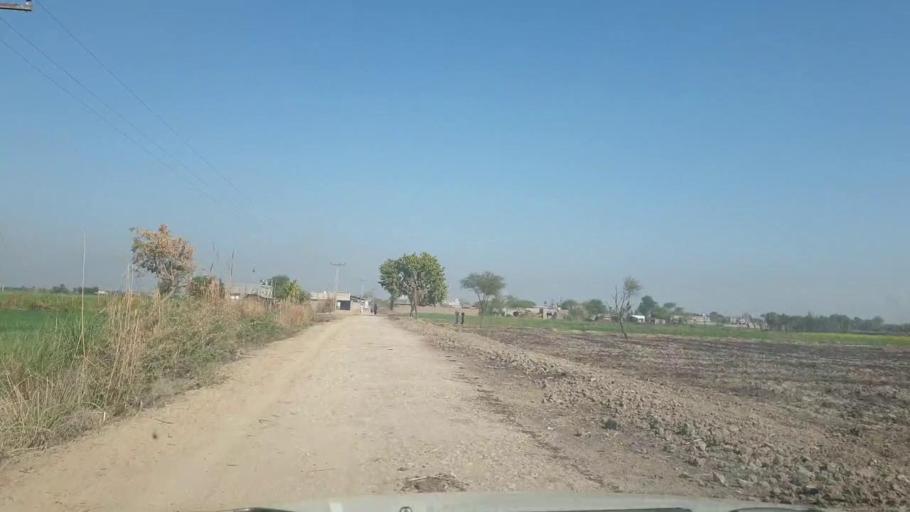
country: PK
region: Sindh
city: Mirpur Khas
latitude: 25.5030
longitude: 69.1547
